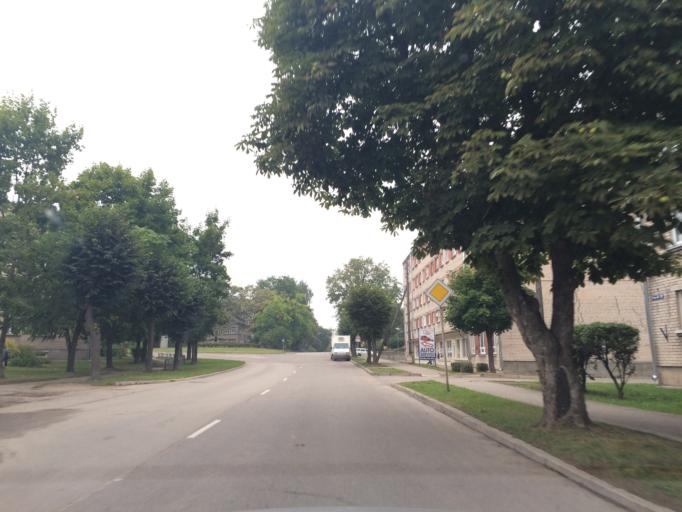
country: LV
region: Rezekne
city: Rezekne
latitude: 56.5018
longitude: 27.3232
